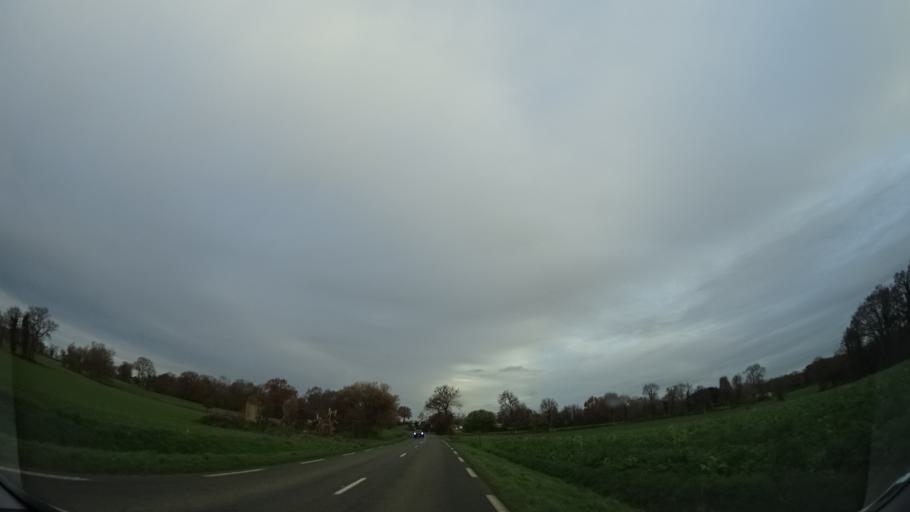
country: FR
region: Brittany
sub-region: Departement des Cotes-d'Armor
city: Evran
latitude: 48.3413
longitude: -1.9659
